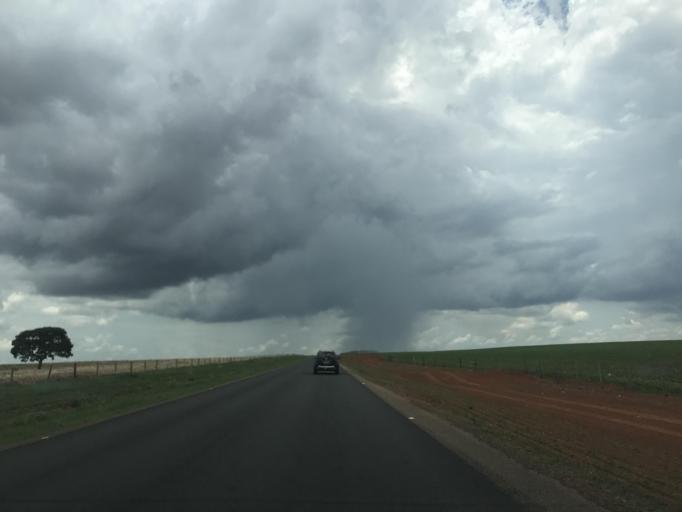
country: BR
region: Goias
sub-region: Vianopolis
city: Vianopolis
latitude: -16.8206
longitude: -48.5257
